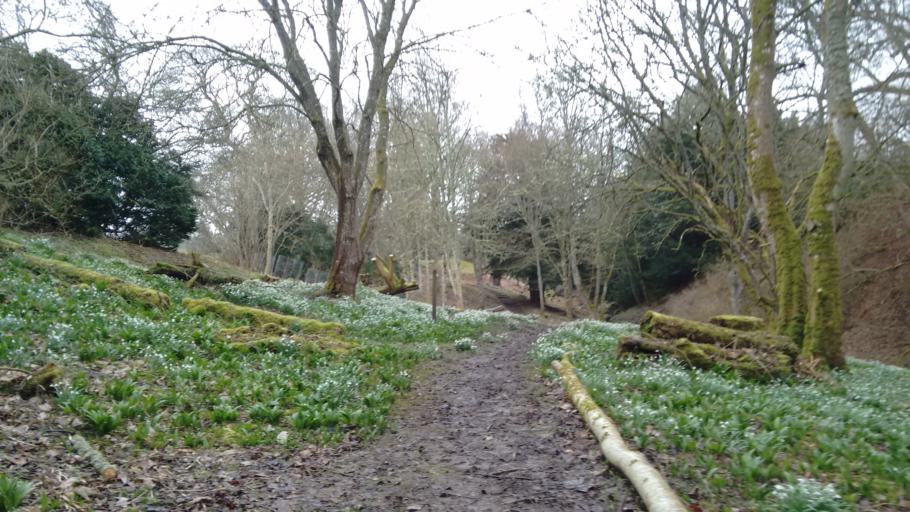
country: GB
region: Scotland
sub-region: Perth and Kinross
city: Perth
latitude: 56.4203
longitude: -3.4360
